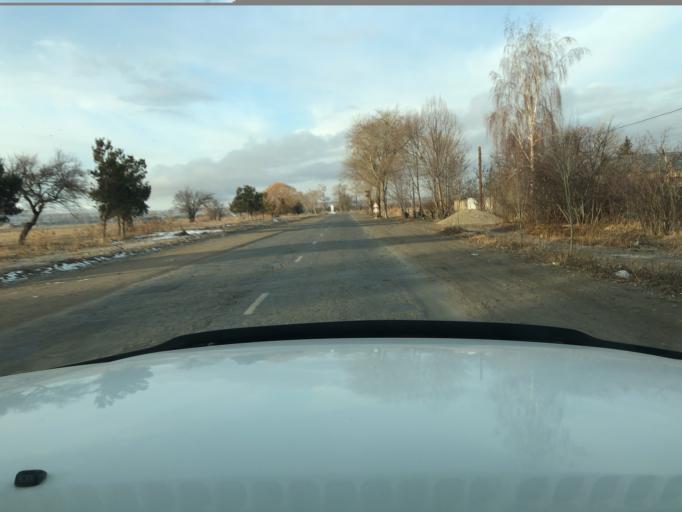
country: KG
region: Ysyk-Koel
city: Karakol
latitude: 42.4817
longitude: 78.3543
